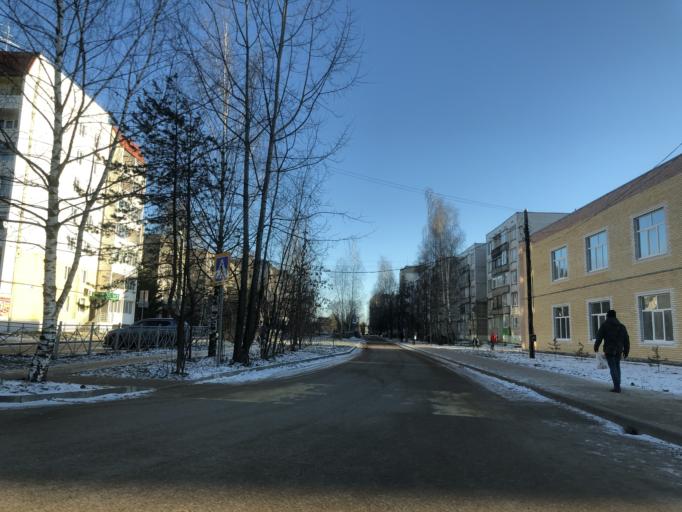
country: RU
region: Tverskaya
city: Rzhev
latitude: 56.2590
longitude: 34.3503
